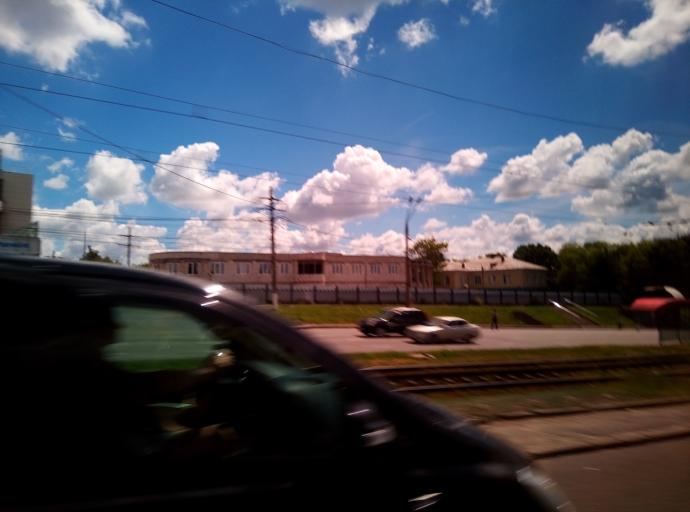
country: RU
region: Kursk
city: Kursk
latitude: 51.7159
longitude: 36.1656
